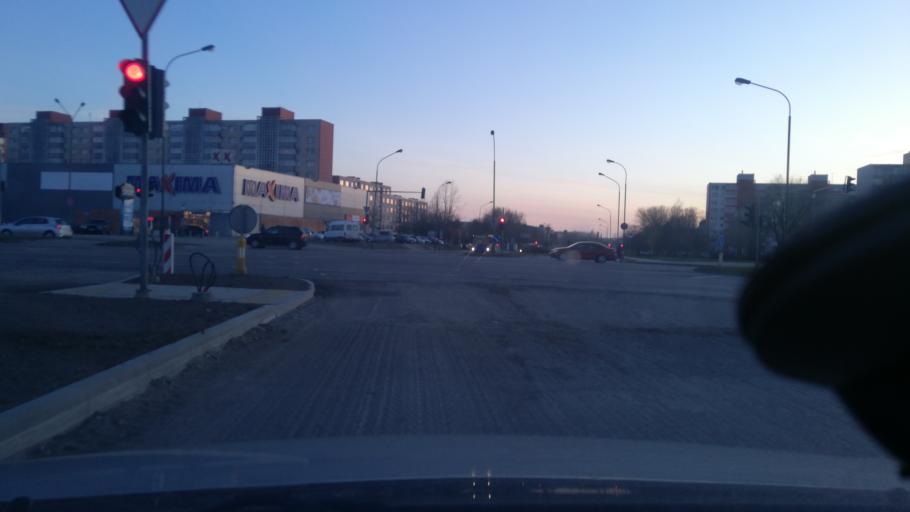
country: LT
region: Klaipedos apskritis
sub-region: Klaipeda
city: Klaipeda
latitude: 55.6776
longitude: 21.1898
